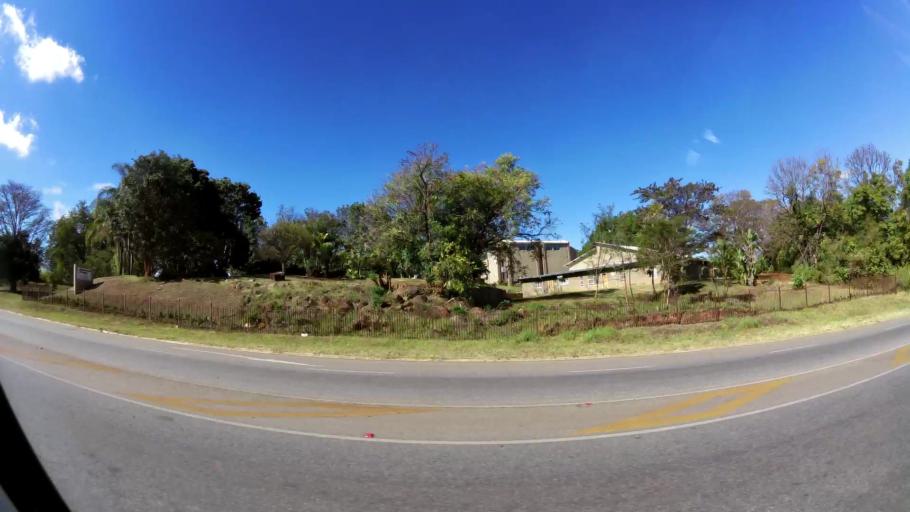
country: ZA
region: Limpopo
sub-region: Mopani District Municipality
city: Tzaneen
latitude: -23.8179
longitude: 30.1689
